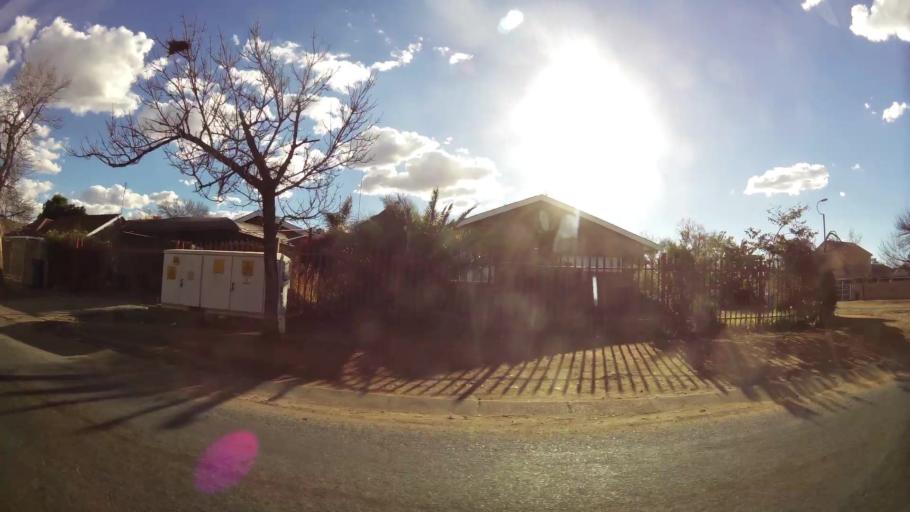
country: ZA
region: North-West
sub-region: Dr Kenneth Kaunda District Municipality
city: Klerksdorp
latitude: -26.8390
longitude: 26.6585
